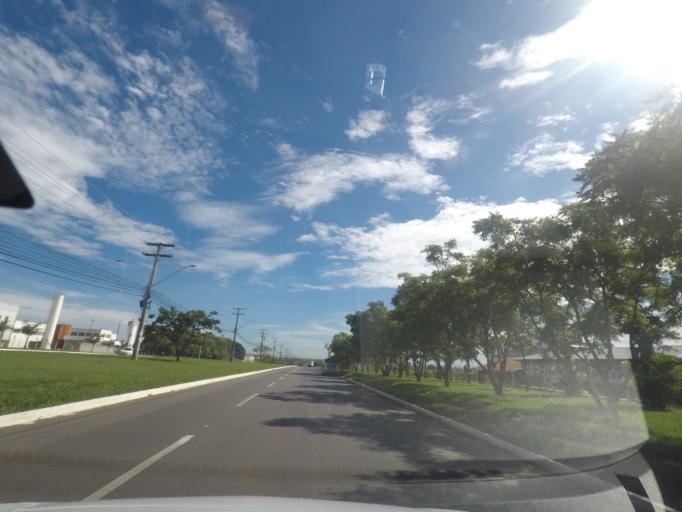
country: BR
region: Goias
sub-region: Aparecida De Goiania
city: Aparecida de Goiania
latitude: -16.7954
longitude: -49.2544
